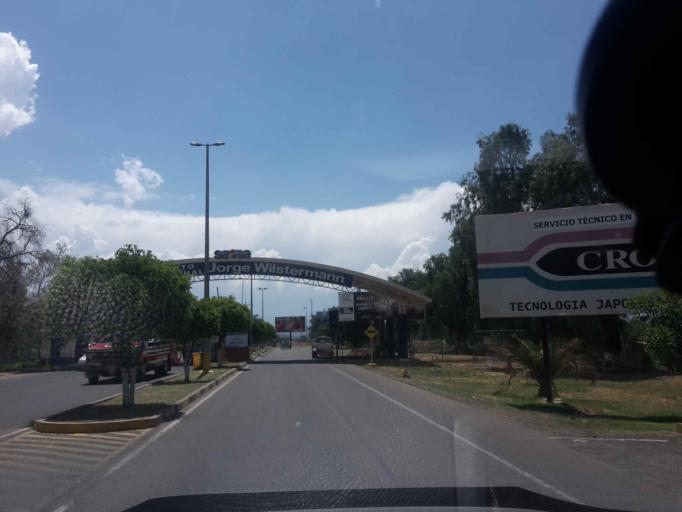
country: BO
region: Cochabamba
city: Cochabamba
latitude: -17.4124
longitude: -66.1776
